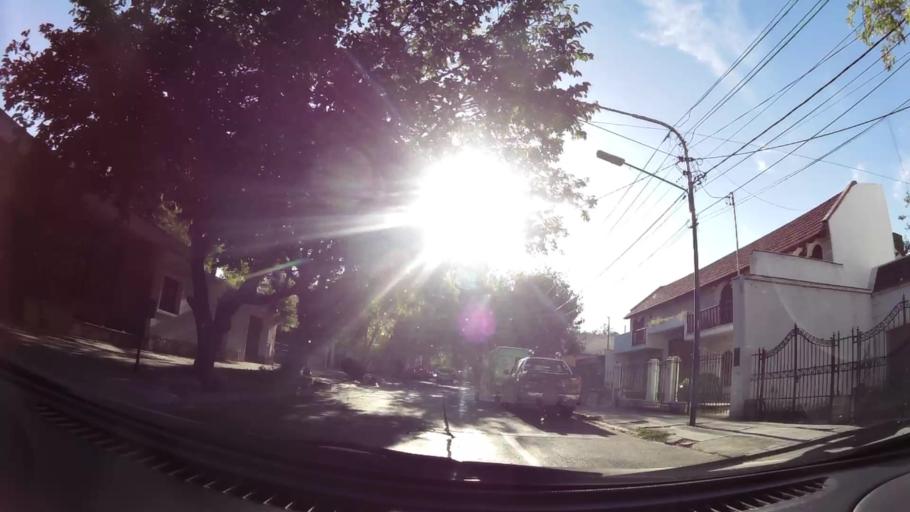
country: AR
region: Mendoza
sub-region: Departamento de Godoy Cruz
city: Godoy Cruz
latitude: -32.9121
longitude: -68.8440
